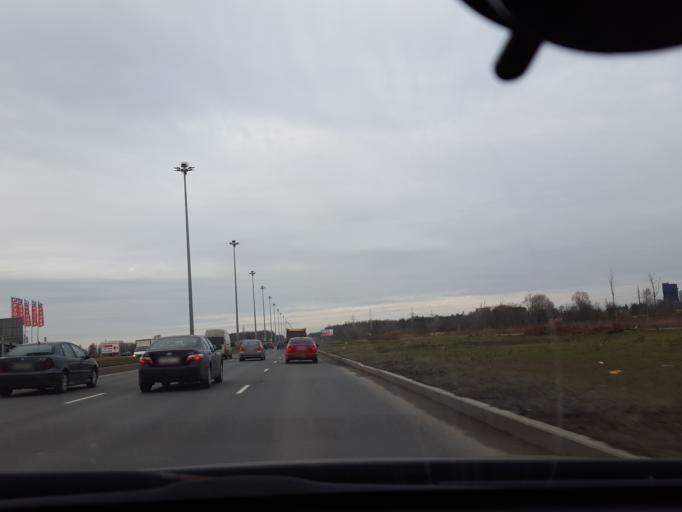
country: RU
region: Leningrad
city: Untolovo
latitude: 60.0389
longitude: 30.2434
